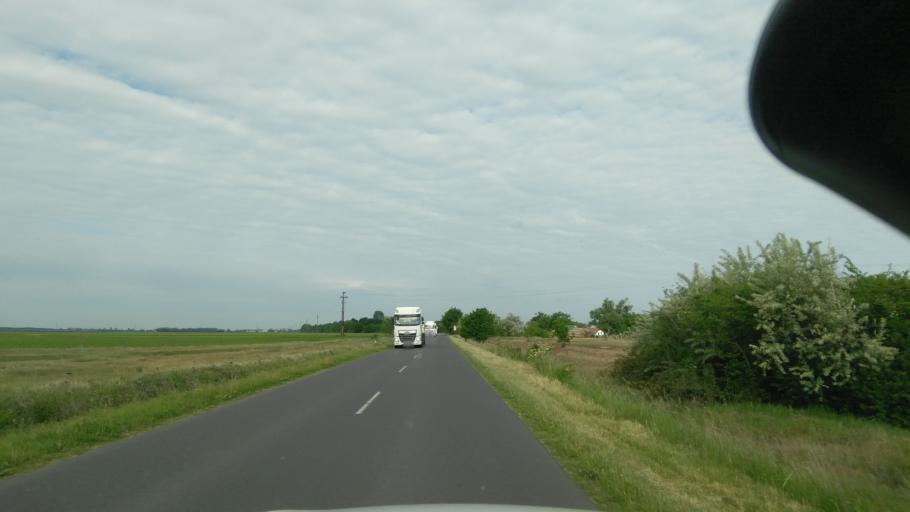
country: HU
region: Bekes
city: Ketegyhaza
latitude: 46.5395
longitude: 21.1525
